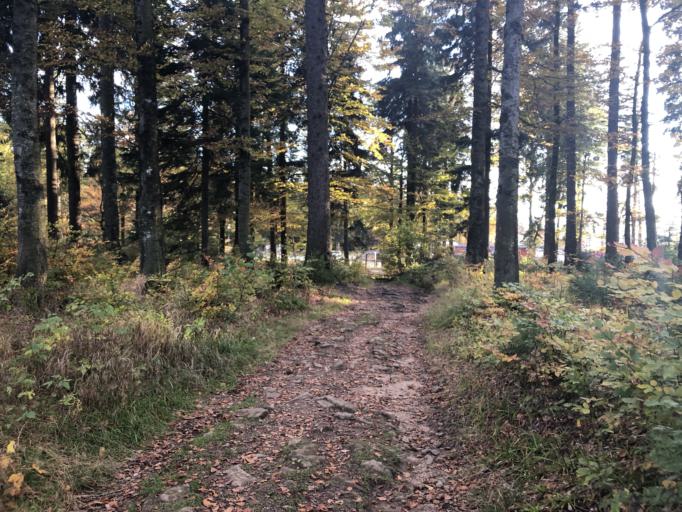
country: DE
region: Bavaria
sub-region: Lower Bavaria
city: Bodenmais
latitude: 49.0752
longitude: 13.1567
